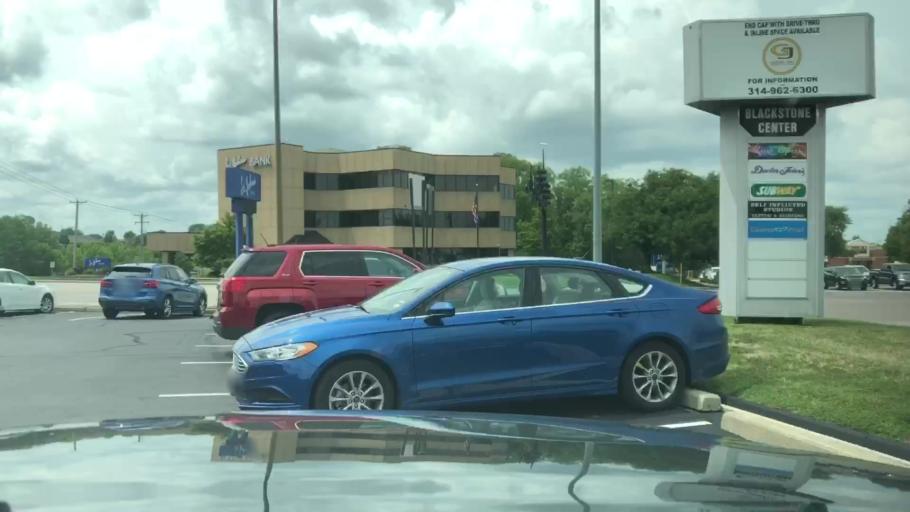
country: US
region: Missouri
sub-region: Saint Charles County
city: Saint Peters
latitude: 38.7917
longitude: -90.5653
